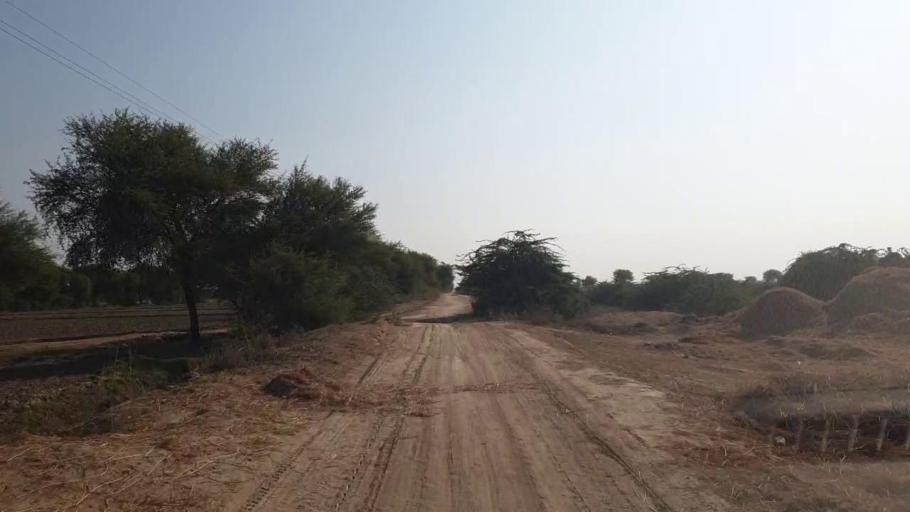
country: PK
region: Sindh
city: Kario
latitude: 24.8879
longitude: 68.6484
